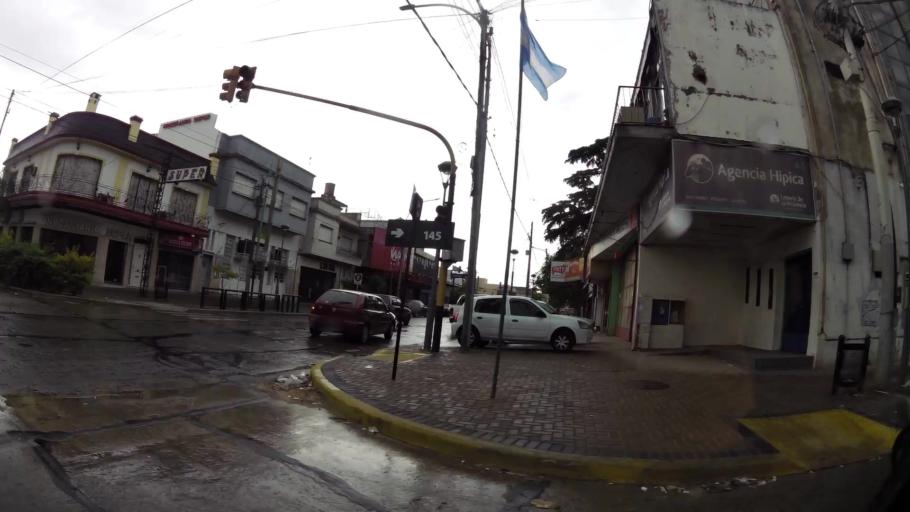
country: AR
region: Buenos Aires
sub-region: Partido de Quilmes
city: Quilmes
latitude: -34.7633
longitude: -58.2123
